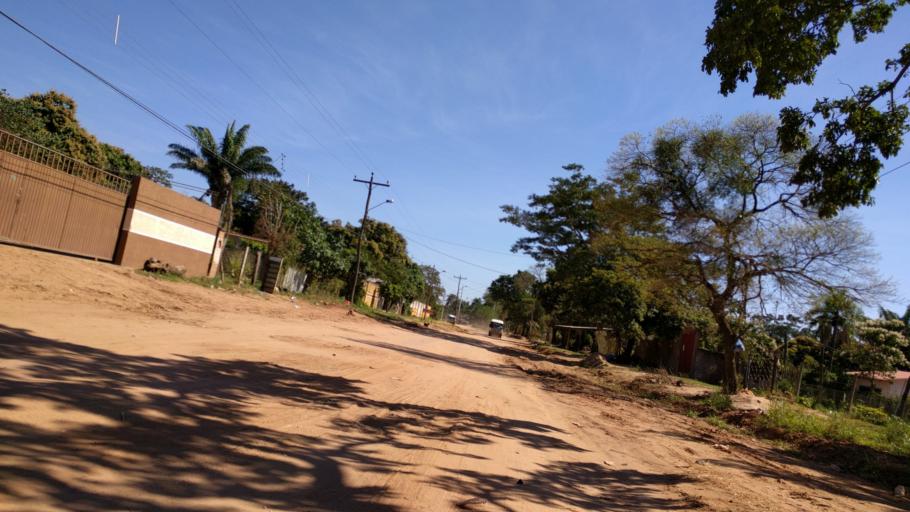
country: BO
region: Santa Cruz
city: Santa Cruz de la Sierra
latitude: -17.8550
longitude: -63.2149
